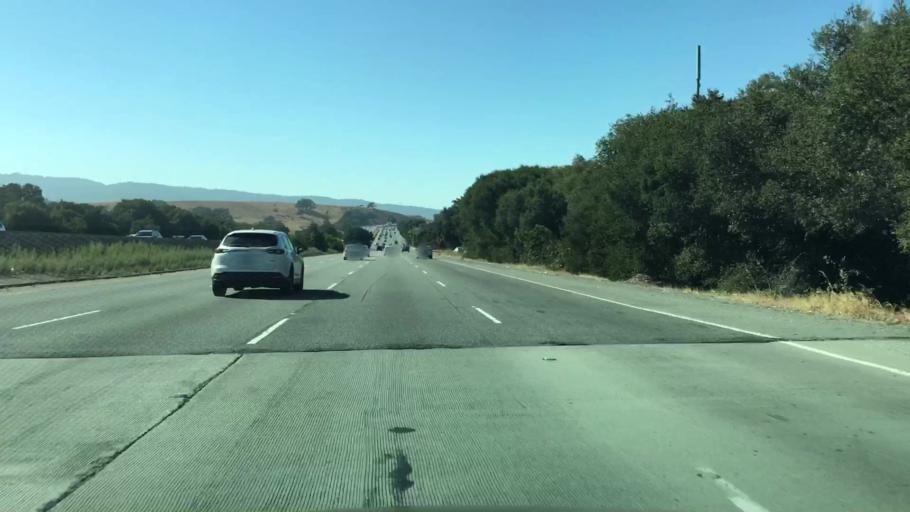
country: US
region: California
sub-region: San Mateo County
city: Ladera
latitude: 37.4083
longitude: -122.1967
